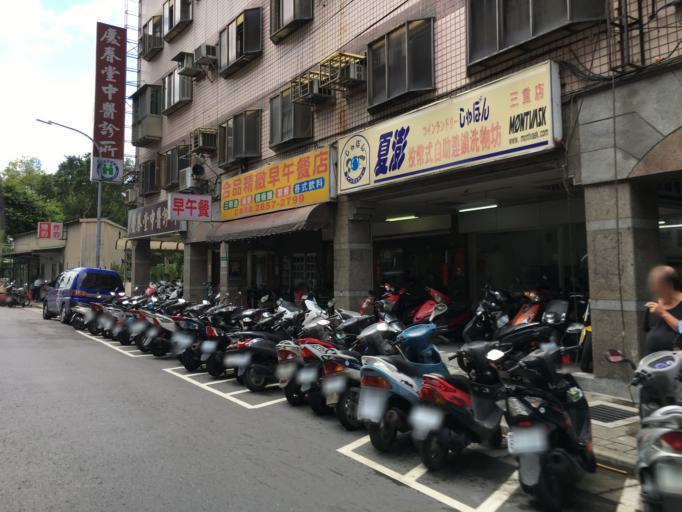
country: TW
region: Taipei
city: Taipei
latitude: 25.0845
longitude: 121.4879
